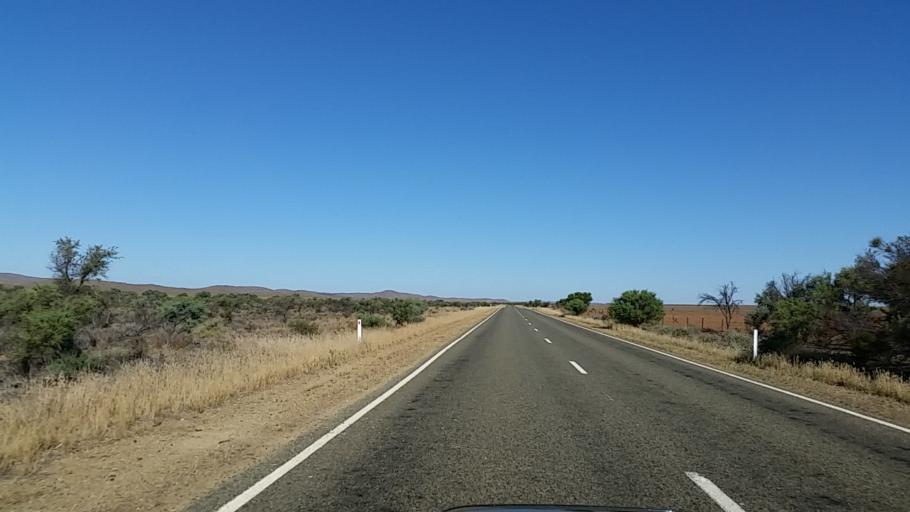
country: AU
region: South Australia
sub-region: Flinders Ranges
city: Quorn
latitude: -32.3971
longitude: 138.5118
